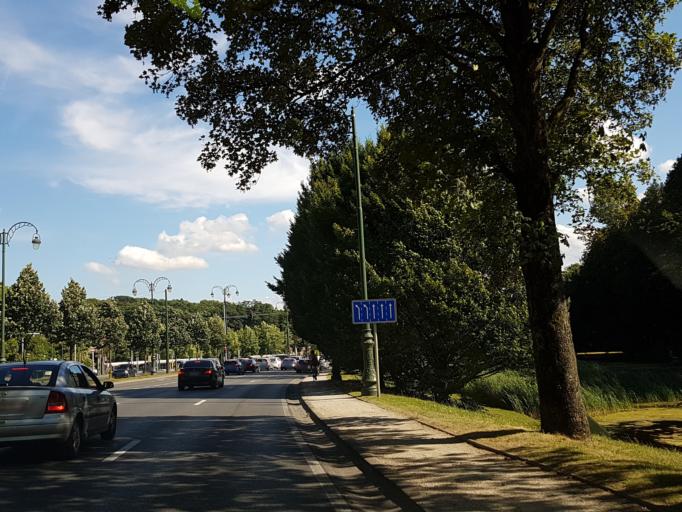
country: BE
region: Flanders
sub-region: Provincie Vlaams-Brabant
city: Kraainem
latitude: 50.8338
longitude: 4.4306
